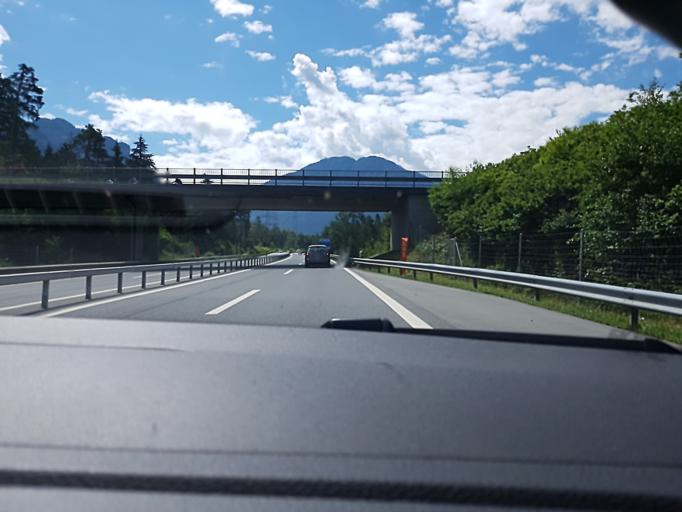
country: CH
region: Grisons
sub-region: Hinterrhein District
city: Cazis
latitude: 46.7378
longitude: 9.4358
